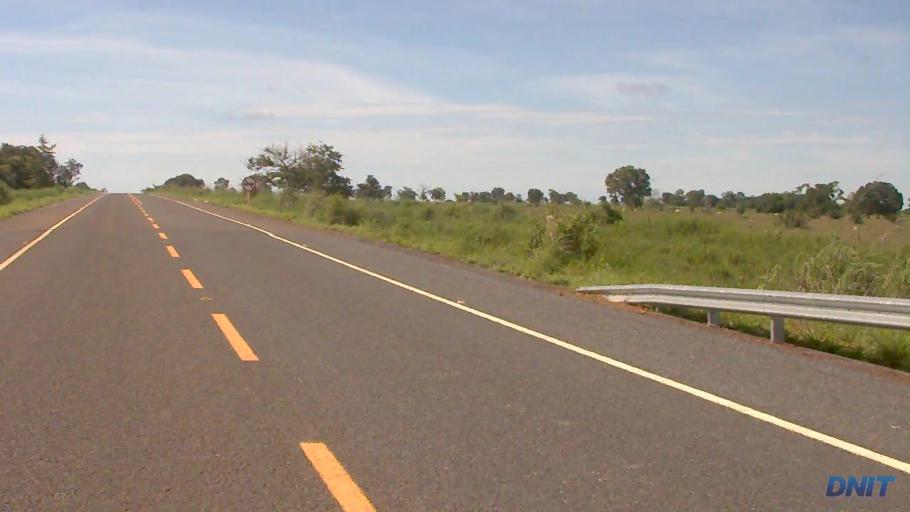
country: BR
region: Goias
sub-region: Sao Miguel Do Araguaia
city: Sao Miguel do Araguaia
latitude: -13.4543
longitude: -50.1196
